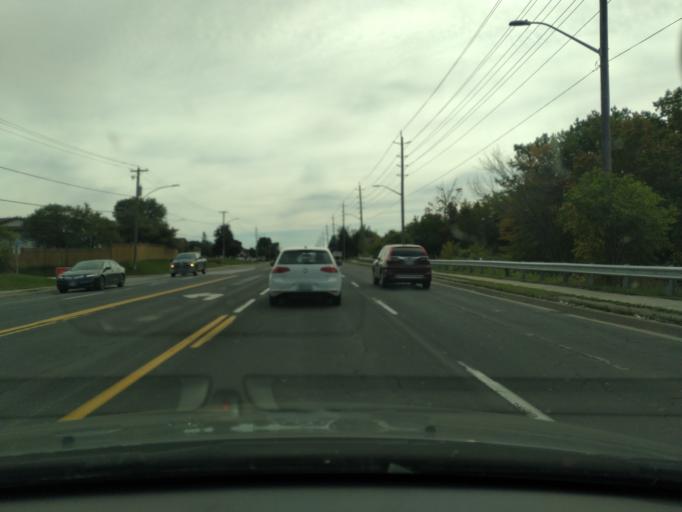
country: CA
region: Ontario
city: Oshawa
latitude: 43.8817
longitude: -78.9109
